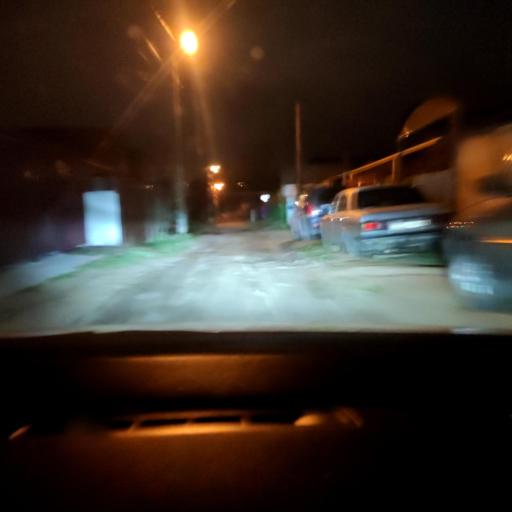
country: RU
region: Voronezj
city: Podgornoye
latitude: 51.7378
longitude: 39.1470
